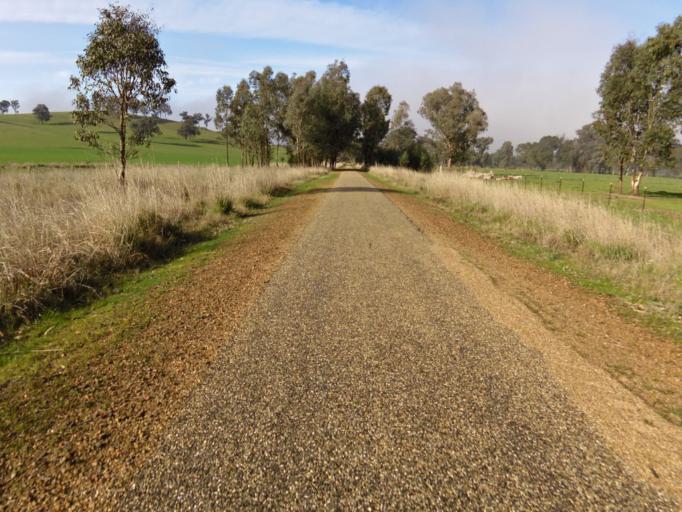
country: AU
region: Victoria
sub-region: Wangaratta
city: Wangaratta
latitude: -36.4424
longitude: 146.5511
